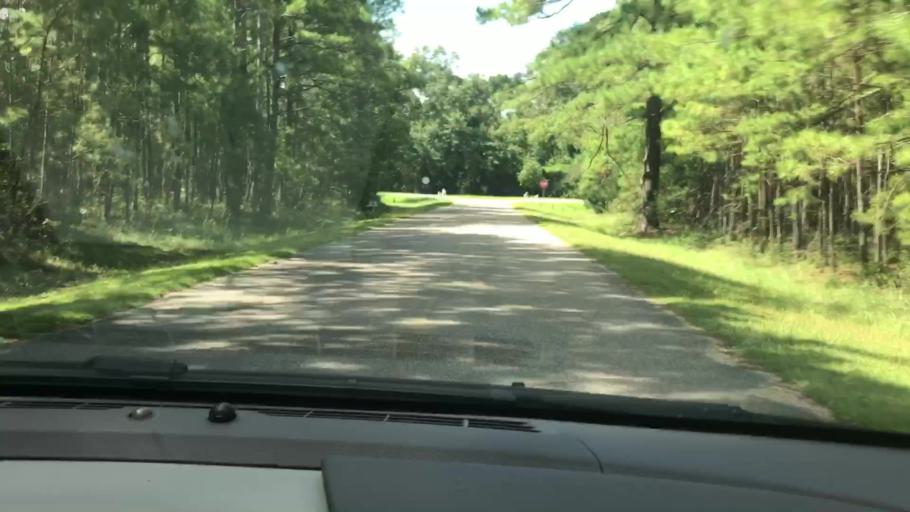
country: US
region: Georgia
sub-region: Clay County
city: Fort Gaines
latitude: 31.7449
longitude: -85.0799
